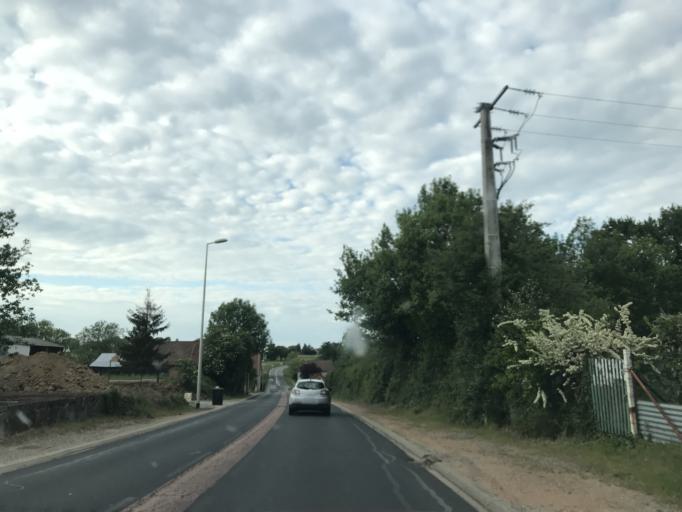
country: FR
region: Auvergne
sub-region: Departement du Puy-de-Dome
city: Randan
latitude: 46.0436
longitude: 3.3618
